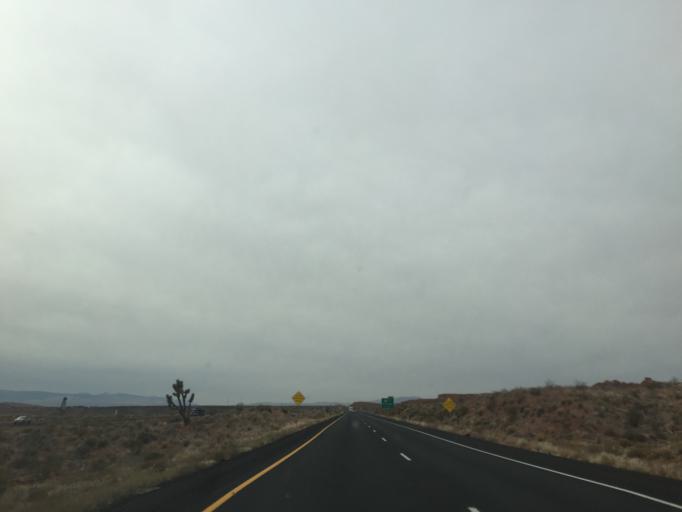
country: US
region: Utah
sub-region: Washington County
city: Washington
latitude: 37.1714
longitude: -113.4413
